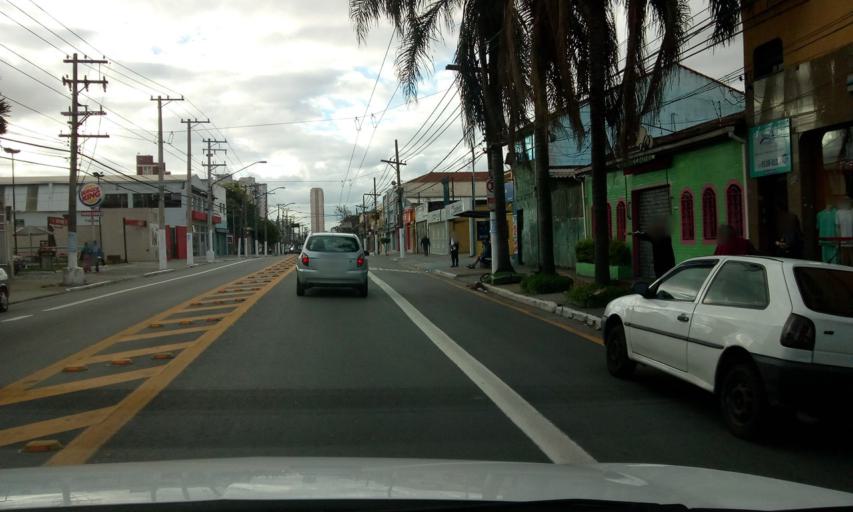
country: BR
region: Sao Paulo
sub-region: Sao Caetano Do Sul
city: Sao Caetano do Sul
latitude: -23.5668
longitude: -46.5112
